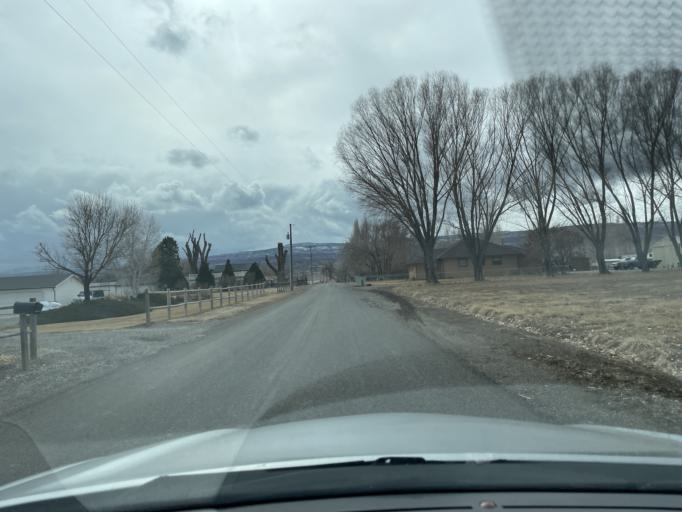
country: US
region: Colorado
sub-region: Mesa County
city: Loma
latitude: 39.1834
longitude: -108.8037
